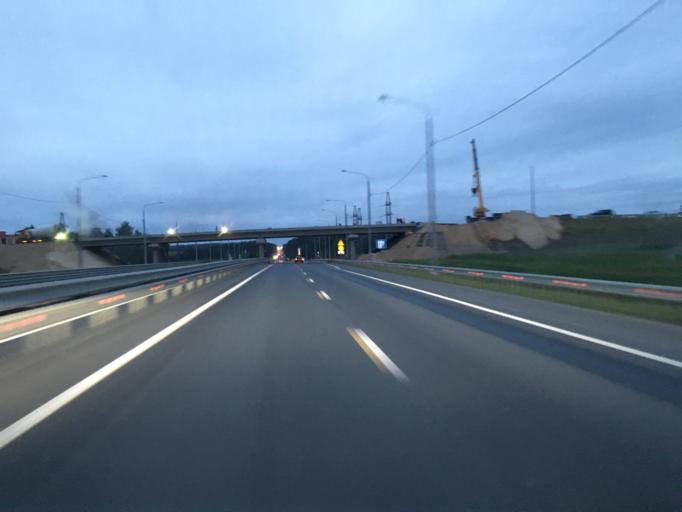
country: RU
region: Kaluga
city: Maloyaroslavets
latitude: 54.9558
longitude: 36.4551
